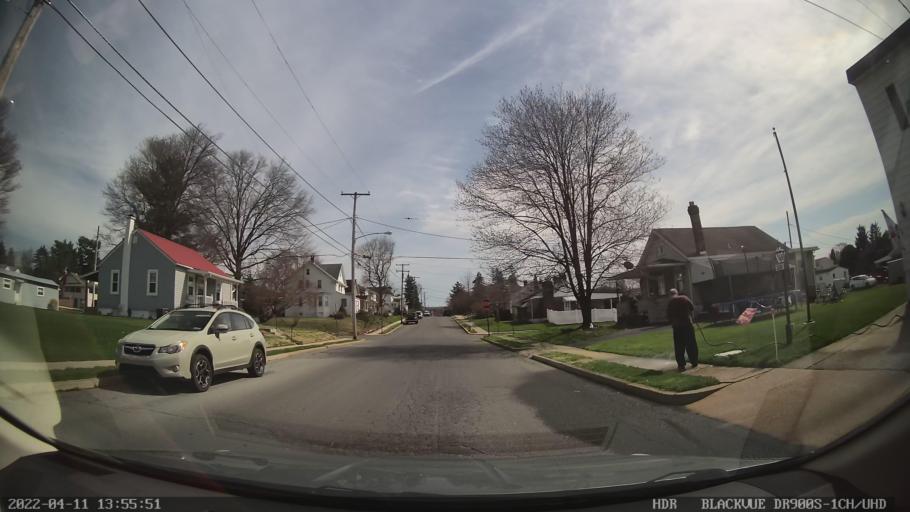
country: US
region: Pennsylvania
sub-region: Berks County
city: Laureldale
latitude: 40.3925
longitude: -75.9119
